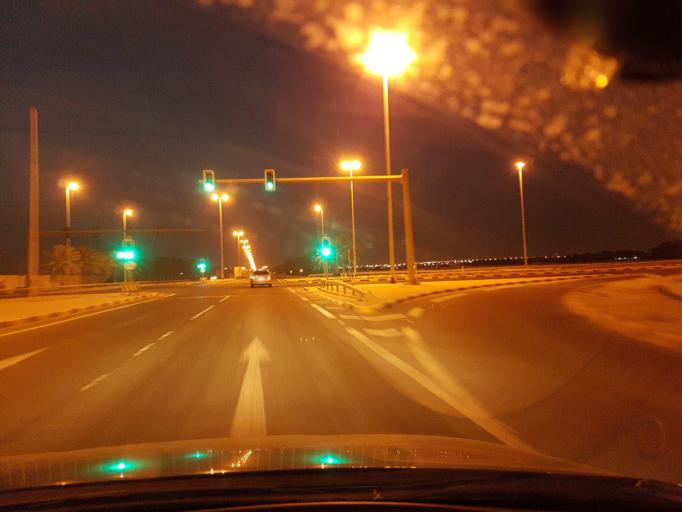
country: BH
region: Central Governorate
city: Dar Kulayb
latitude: 26.0376
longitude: 50.5000
